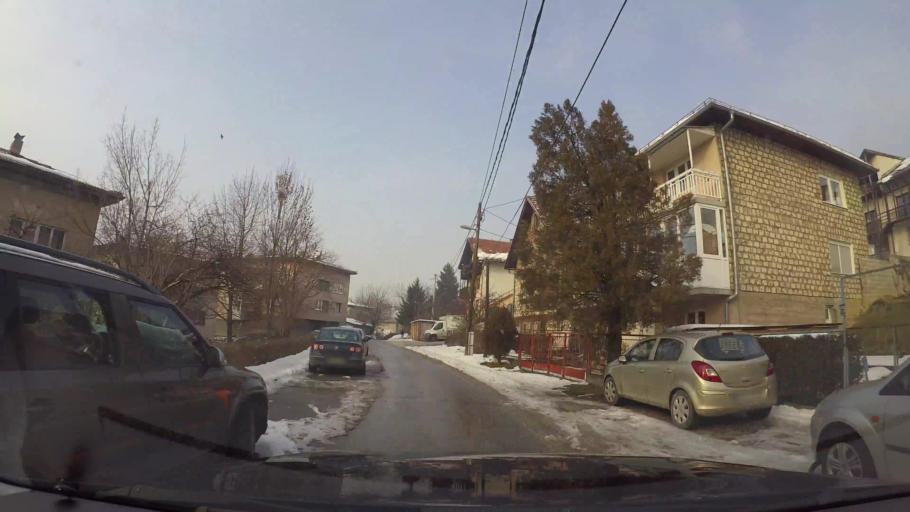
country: BA
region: Federation of Bosnia and Herzegovina
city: Kobilja Glava
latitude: 43.8727
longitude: 18.4148
